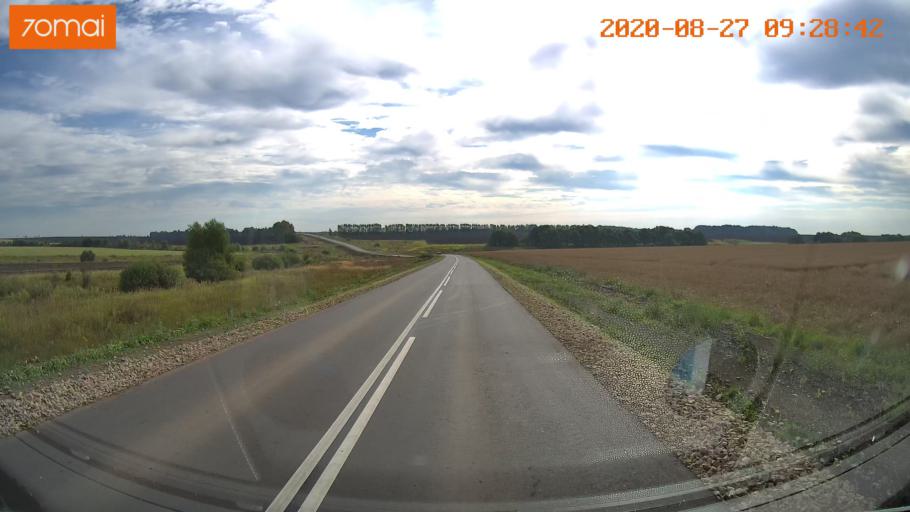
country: RU
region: Tula
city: Kazachka
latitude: 53.3124
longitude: 38.2059
